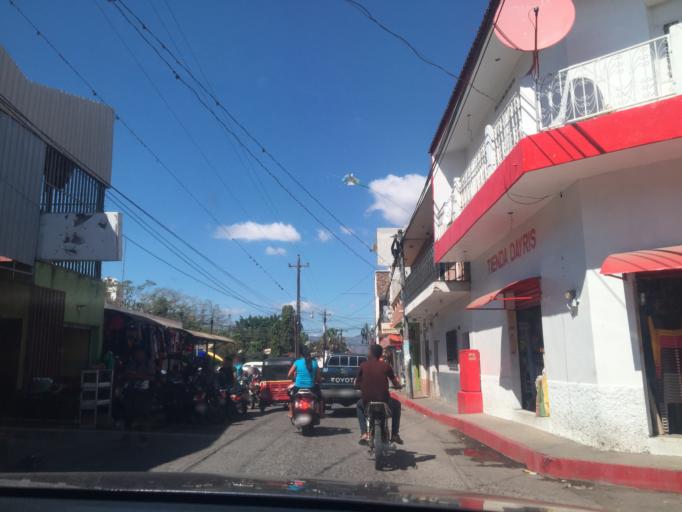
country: GT
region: Chiquimula
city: Ipala
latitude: 14.6195
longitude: -89.6232
